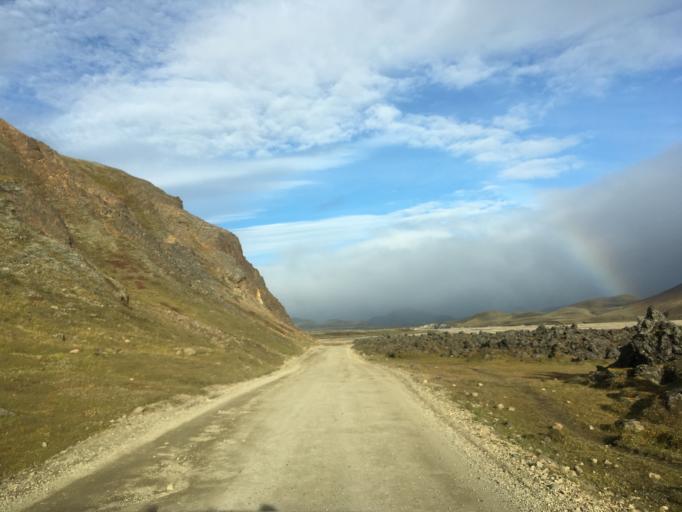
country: IS
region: South
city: Vestmannaeyjar
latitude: 64.0015
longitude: -19.0476
